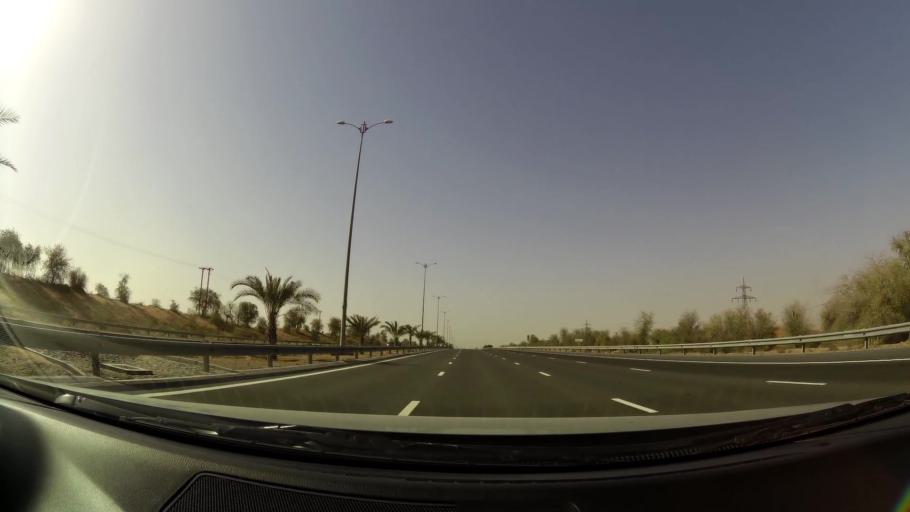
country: OM
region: Al Buraimi
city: Al Buraymi
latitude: 24.5394
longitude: 55.7572
